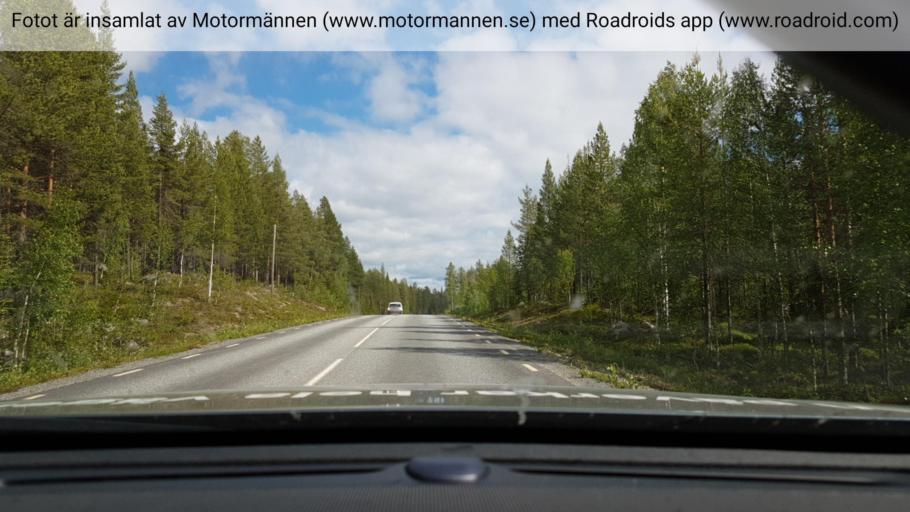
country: SE
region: Vaesterbotten
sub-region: Sorsele Kommun
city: Sorsele
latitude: 65.6909
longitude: 17.1916
